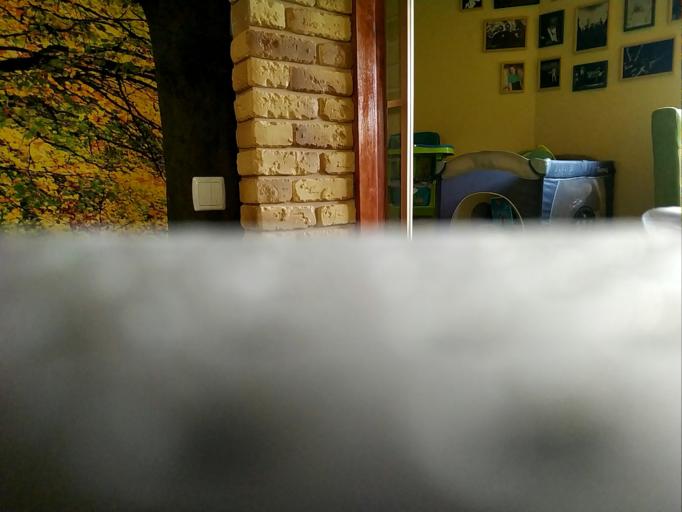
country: RU
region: Kaluga
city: Seredeyskiy
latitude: 53.9763
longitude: 35.3264
